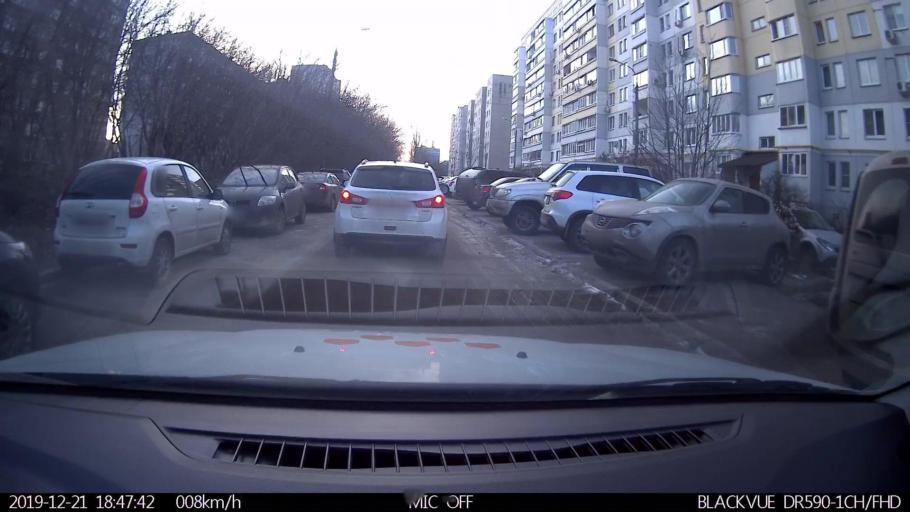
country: RU
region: Nizjnij Novgorod
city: Nizhniy Novgorod
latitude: 56.3278
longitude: 43.9285
